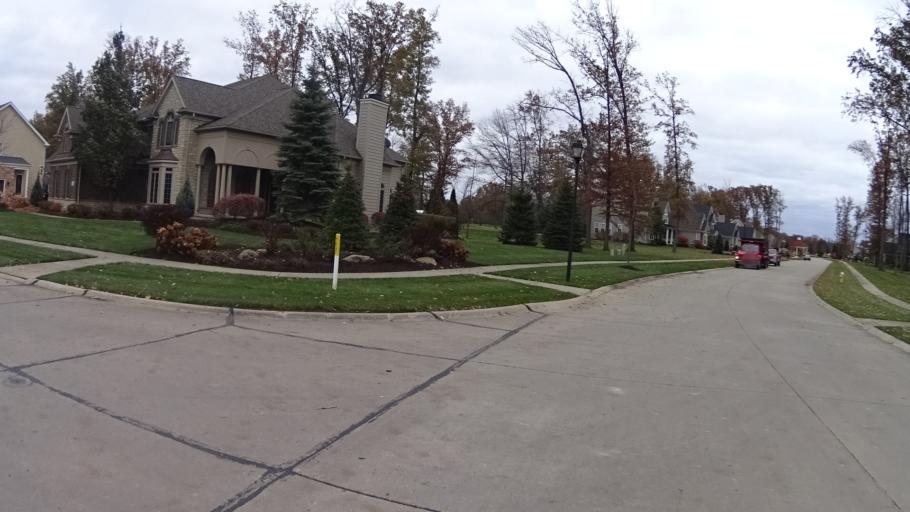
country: US
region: Ohio
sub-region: Lorain County
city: Avon Lake
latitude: 41.4872
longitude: -82.0089
